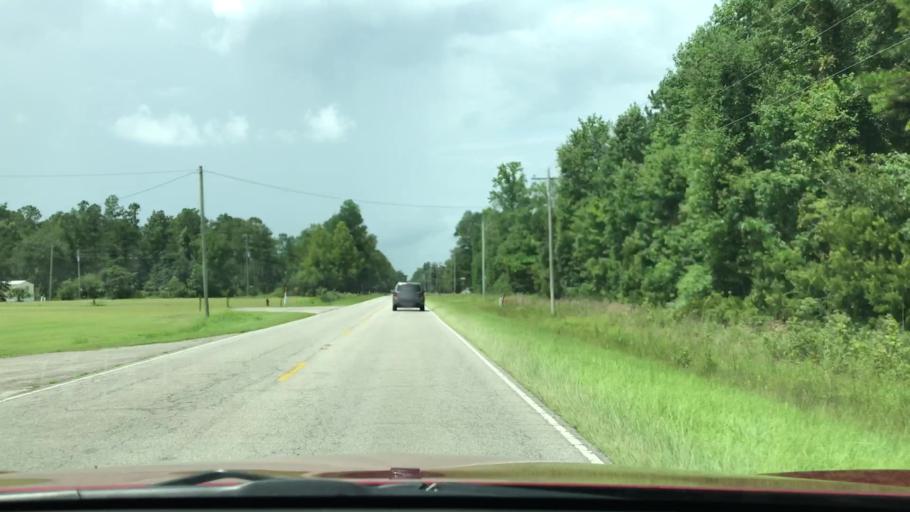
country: US
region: South Carolina
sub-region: Horry County
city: Red Hill
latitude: 33.9024
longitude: -78.9170
